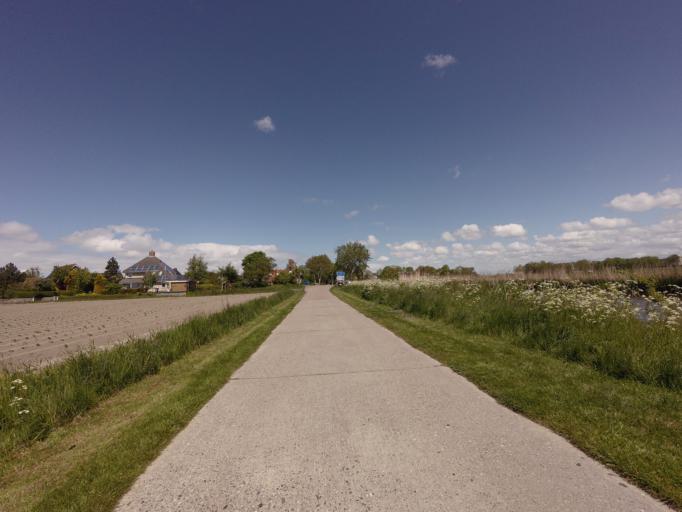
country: NL
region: Friesland
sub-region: Gemeente Harlingen
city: Harlingen
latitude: 53.1385
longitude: 5.4359
